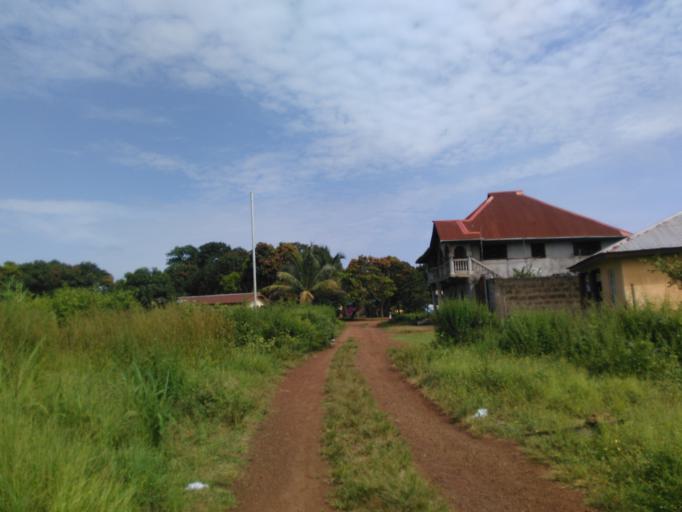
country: SL
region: Southern Province
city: Rotifunk
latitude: 8.4851
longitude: -12.7595
